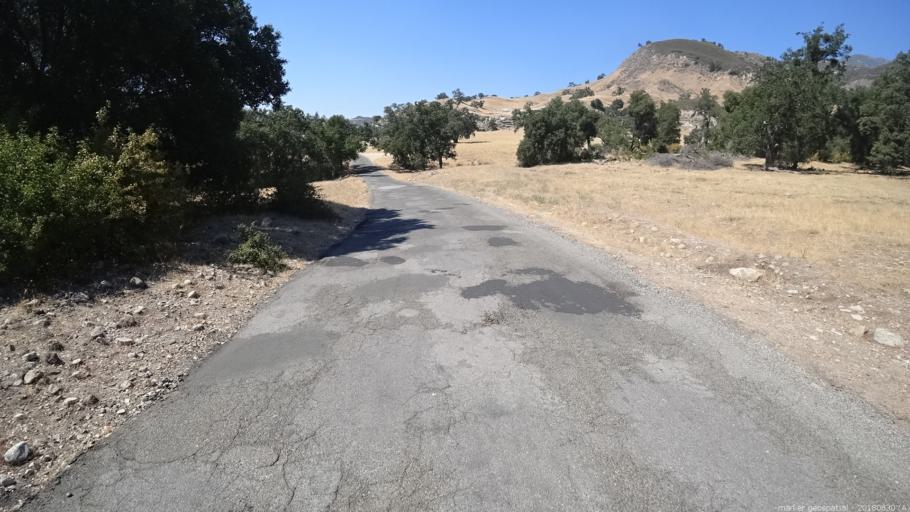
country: US
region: California
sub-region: Monterey County
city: Greenfield
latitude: 36.0989
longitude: -121.4270
